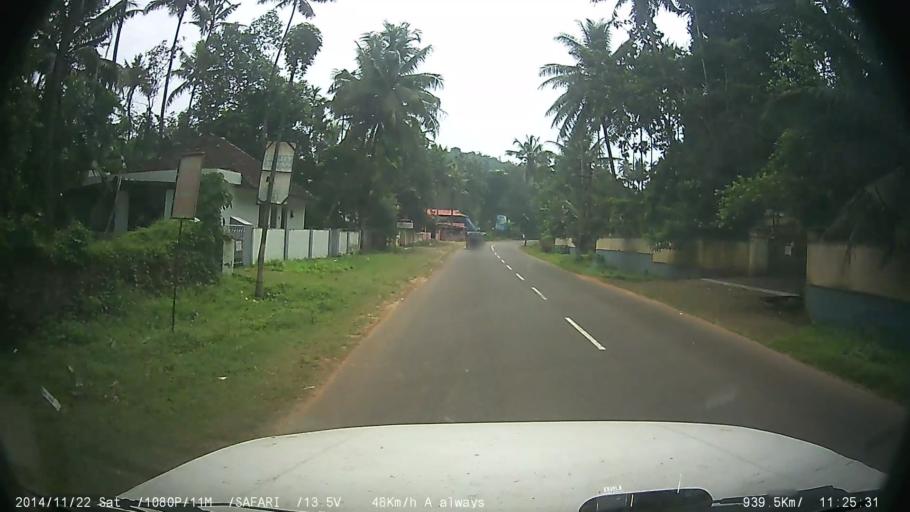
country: IN
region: Kerala
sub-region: Ernakulam
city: Muvattupuzha
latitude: 9.9435
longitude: 76.5750
